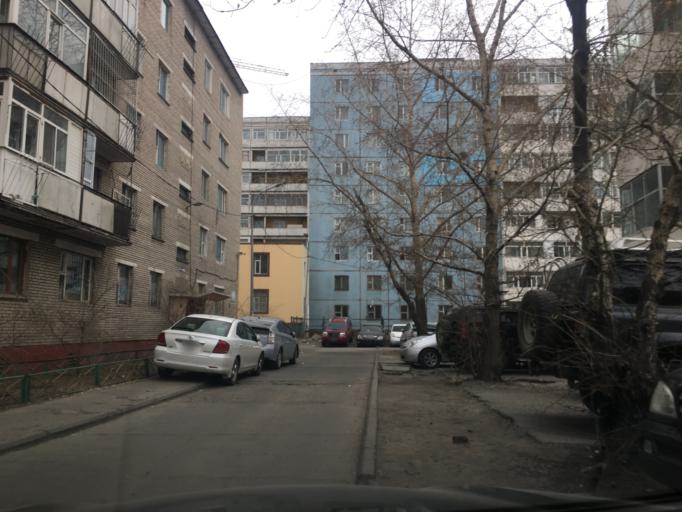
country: MN
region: Ulaanbaatar
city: Ulaanbaatar
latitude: 47.9104
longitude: 106.8876
